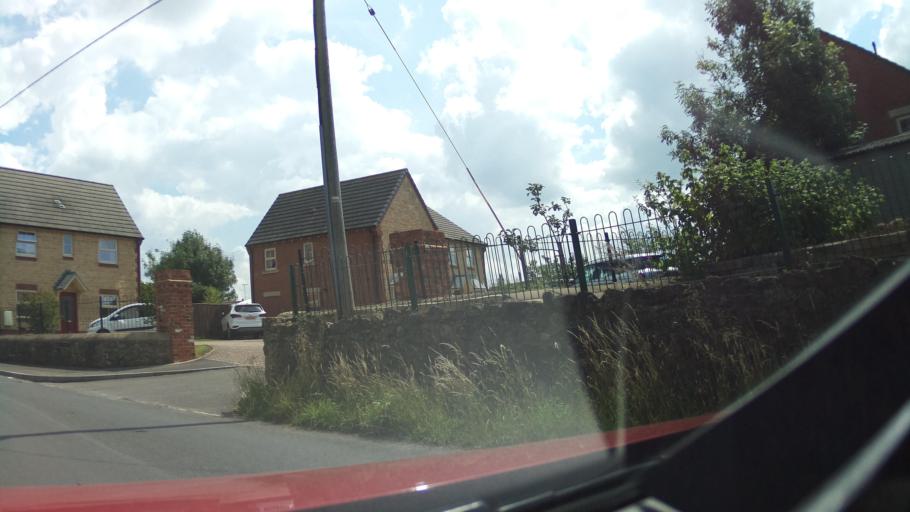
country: GB
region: England
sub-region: Wiltshire
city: Purton
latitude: 51.5869
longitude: -1.8880
